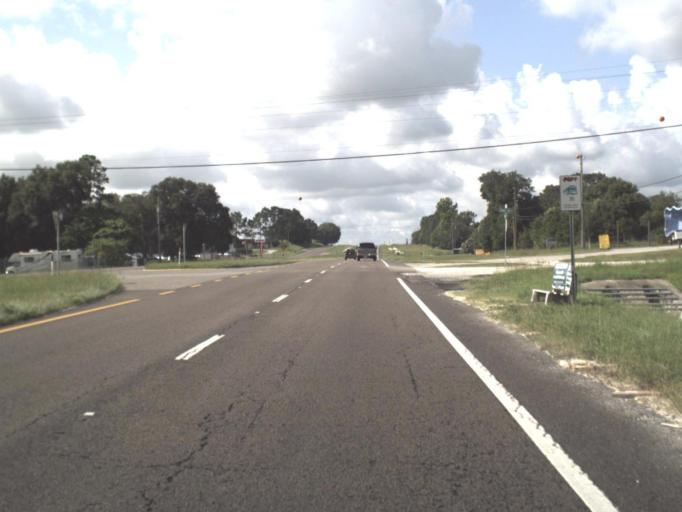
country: US
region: Florida
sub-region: Pasco County
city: Zephyrhills North
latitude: 28.2888
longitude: -82.1879
